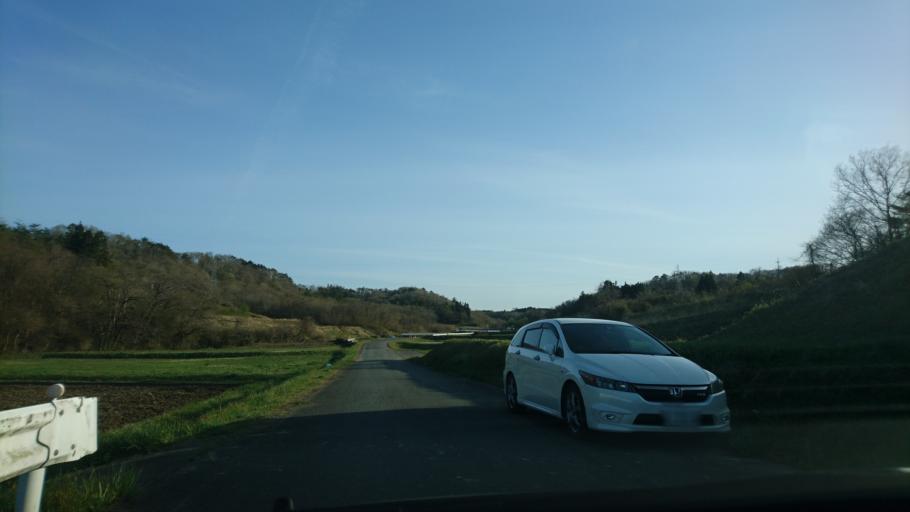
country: JP
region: Iwate
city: Ichinoseki
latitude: 38.8958
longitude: 141.2219
